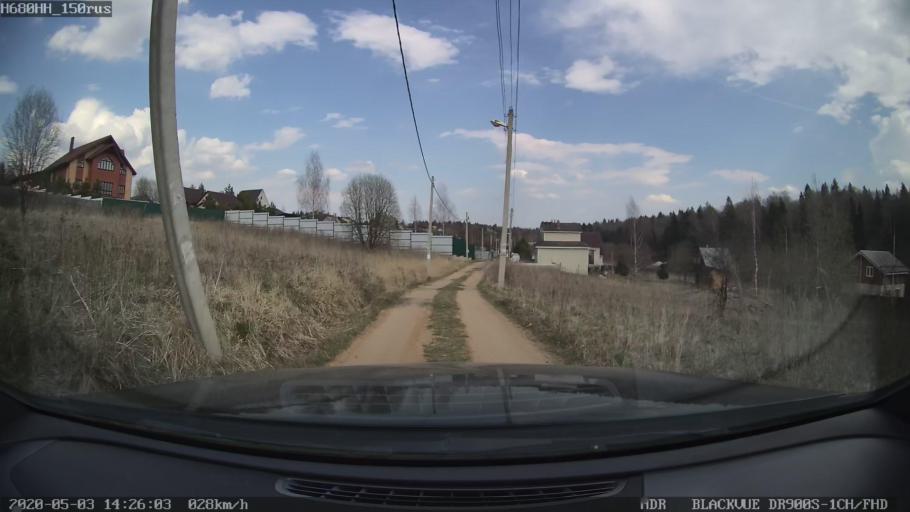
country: RU
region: Moskovskaya
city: Solnechnogorsk
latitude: 56.2508
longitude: 37.0060
